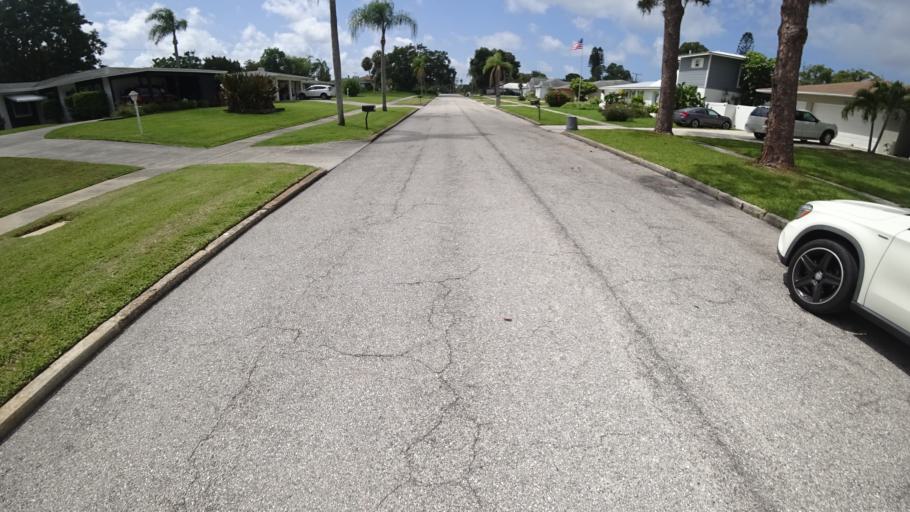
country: US
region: Florida
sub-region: Manatee County
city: Whitfield
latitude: 27.4104
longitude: -82.5725
